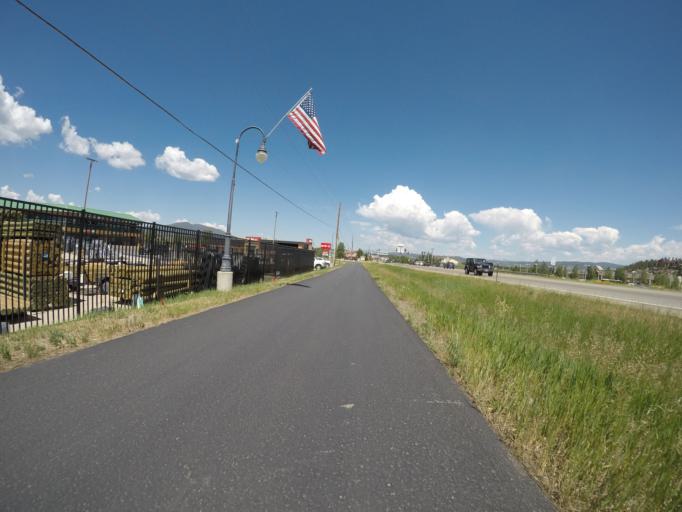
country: US
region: Colorado
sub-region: Grand County
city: Fraser
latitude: 39.9432
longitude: -105.8111
